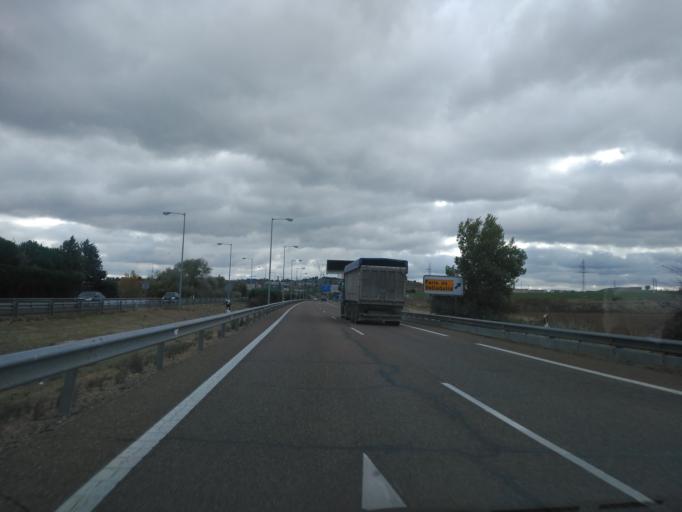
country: ES
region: Castille and Leon
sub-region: Provincia de Valladolid
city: Zaratan
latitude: 41.6682
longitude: -4.7617
